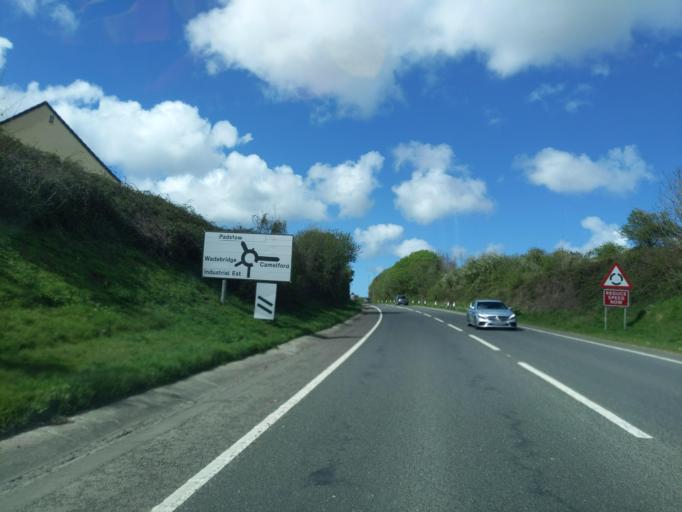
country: GB
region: England
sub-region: Cornwall
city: Wadebridge
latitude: 50.5212
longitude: -4.8204
